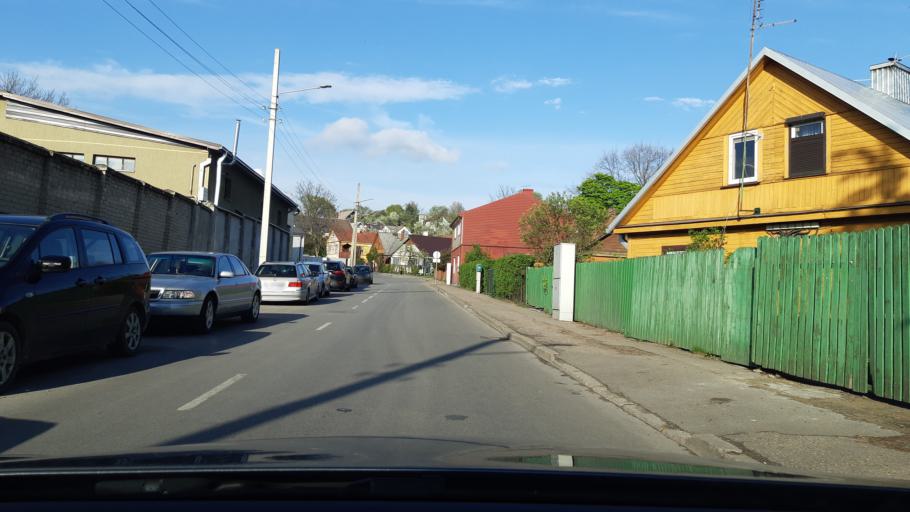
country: LT
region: Kauno apskritis
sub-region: Kaunas
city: Aleksotas
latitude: 54.8741
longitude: 23.9408
